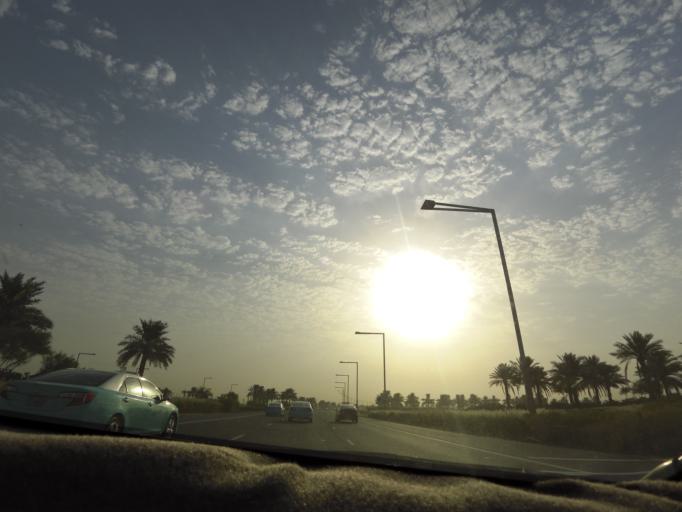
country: QA
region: Al Wakrah
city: Al Wakrah
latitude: 25.2440
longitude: 51.5987
